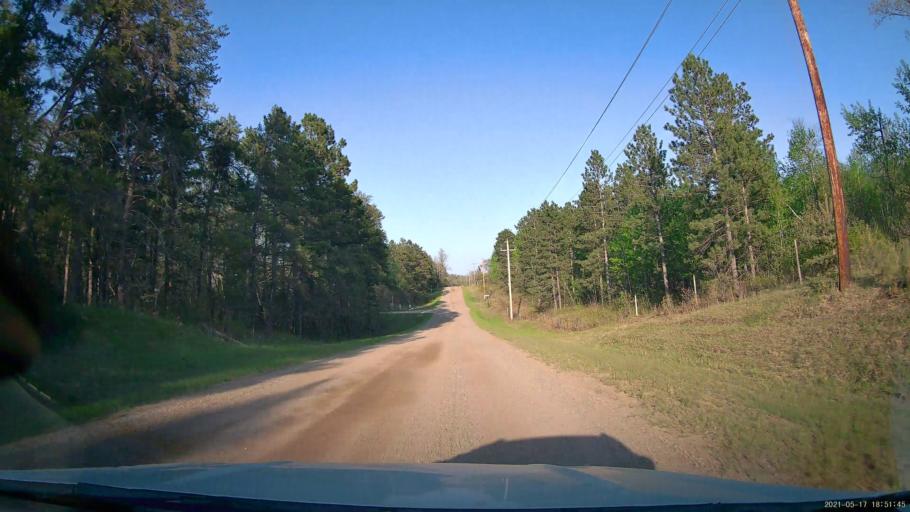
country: US
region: Minnesota
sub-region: Hubbard County
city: Park Rapids
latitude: 46.9438
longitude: -95.0084
